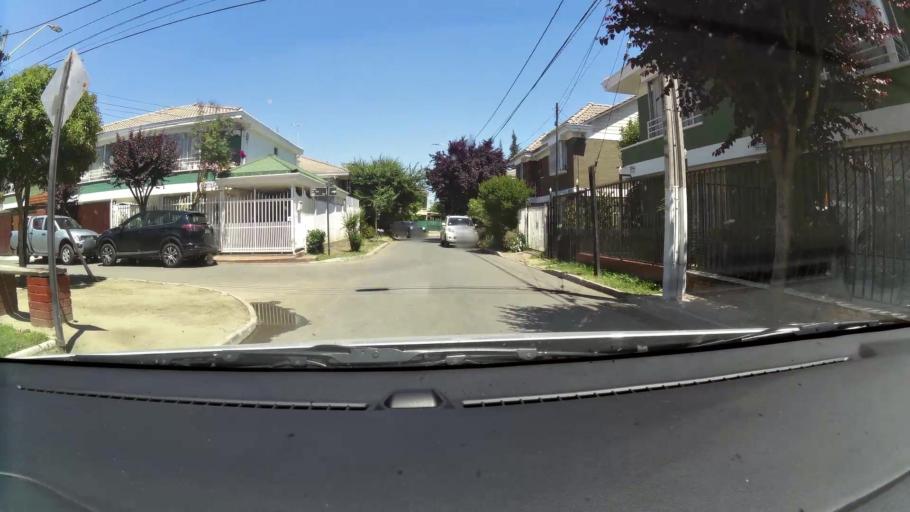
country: CL
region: Santiago Metropolitan
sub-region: Provincia de Maipo
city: San Bernardo
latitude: -33.6200
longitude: -70.7118
